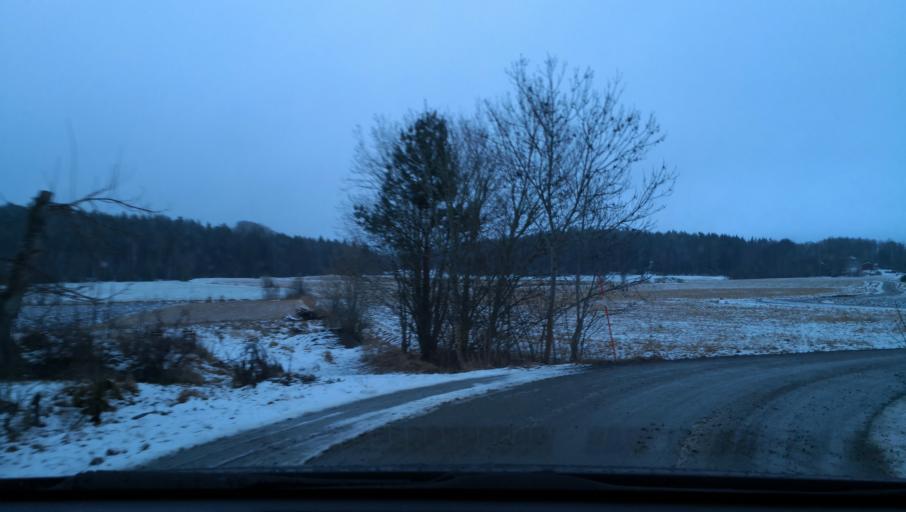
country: SE
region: Vaestmanland
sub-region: Kungsors Kommun
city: Kungsoer
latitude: 59.4013
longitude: 16.2047
